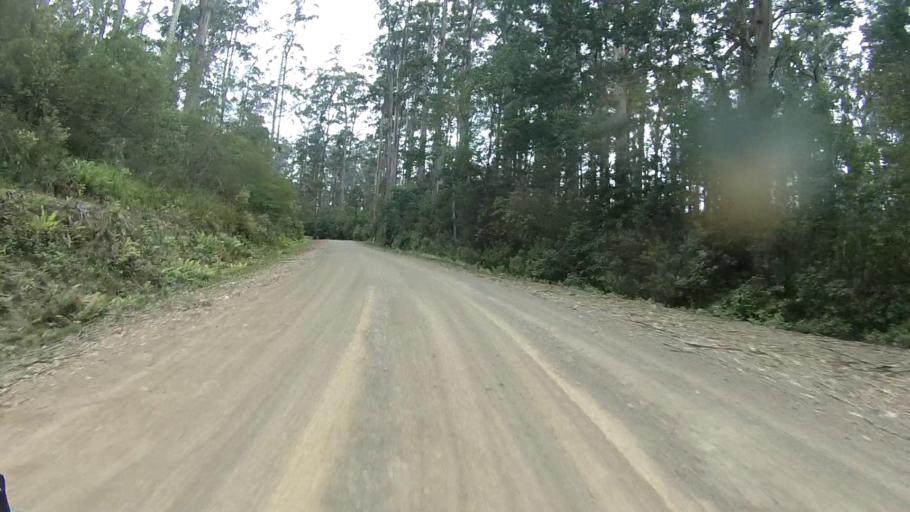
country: AU
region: Tasmania
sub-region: Sorell
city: Sorell
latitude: -42.7034
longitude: 147.8563
